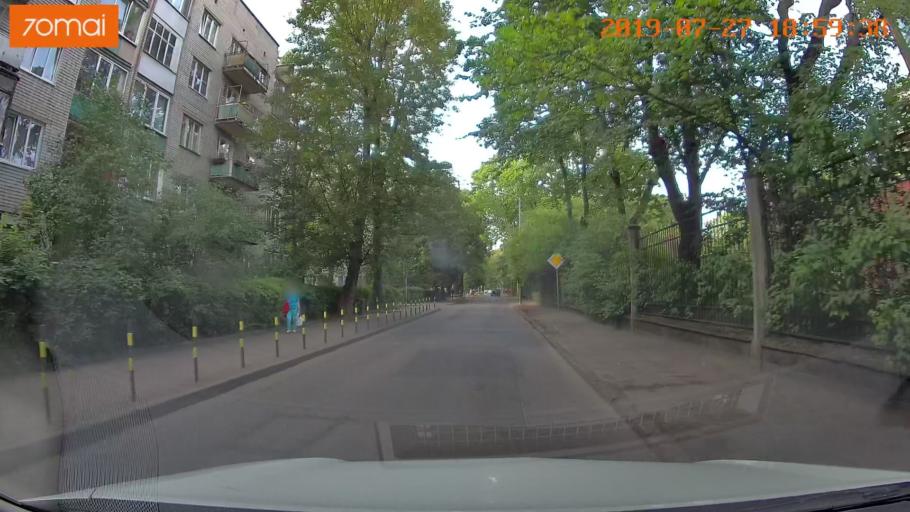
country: RU
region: Kaliningrad
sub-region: Gorod Kaliningrad
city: Kaliningrad
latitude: 54.7231
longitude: 20.4849
